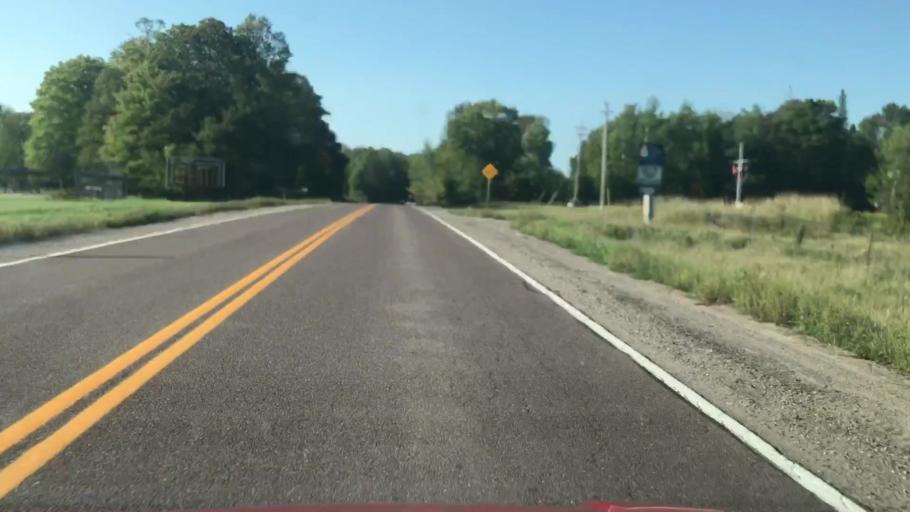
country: US
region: Michigan
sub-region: Chippewa County
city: Sault Ste. Marie
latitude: 46.2780
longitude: -84.0296
